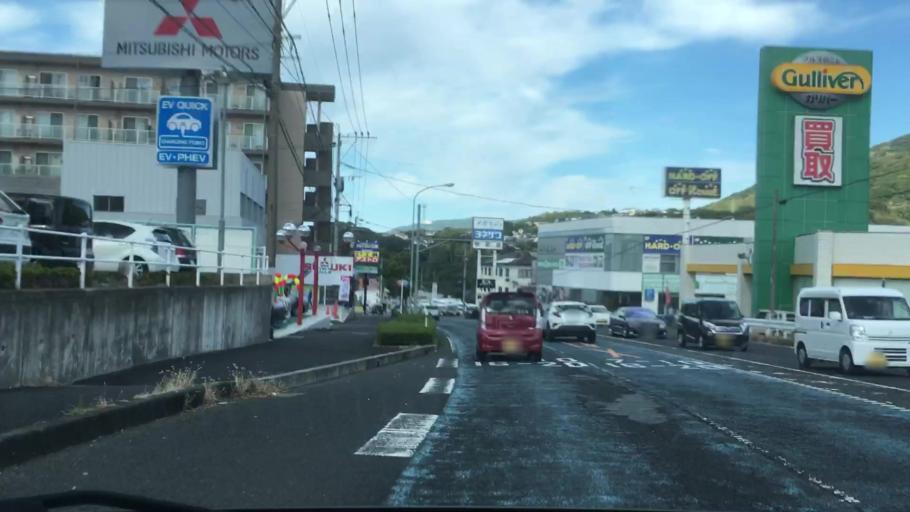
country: JP
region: Nagasaki
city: Sasebo
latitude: 33.1581
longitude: 129.7651
